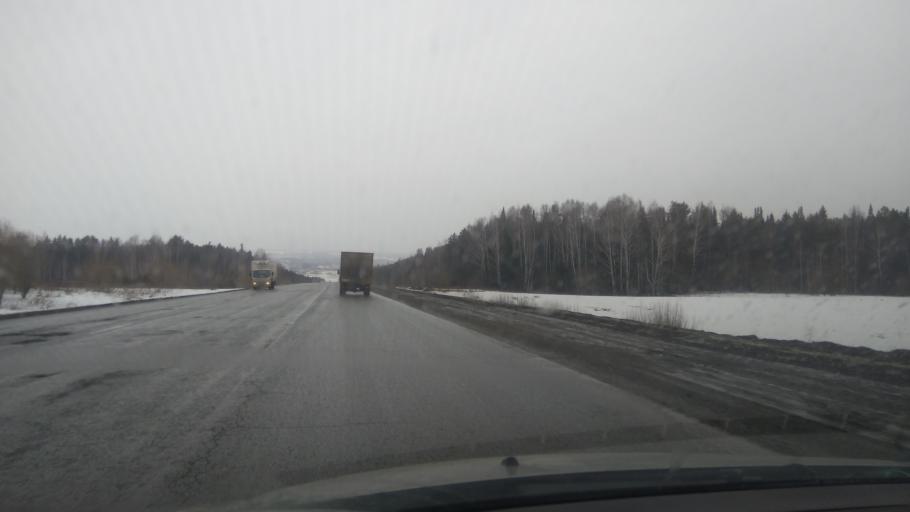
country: RU
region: Perm
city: Kungur
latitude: 57.3471
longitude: 56.9391
